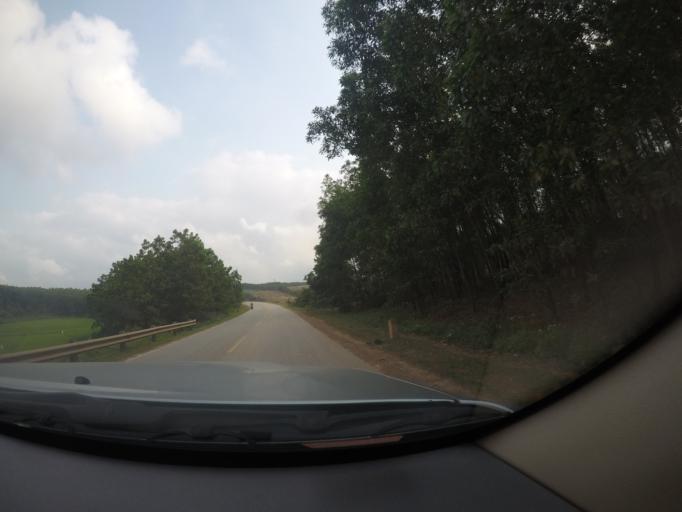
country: VN
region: Quang Binh
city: Kien Giang
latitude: 17.1102
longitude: 106.8369
